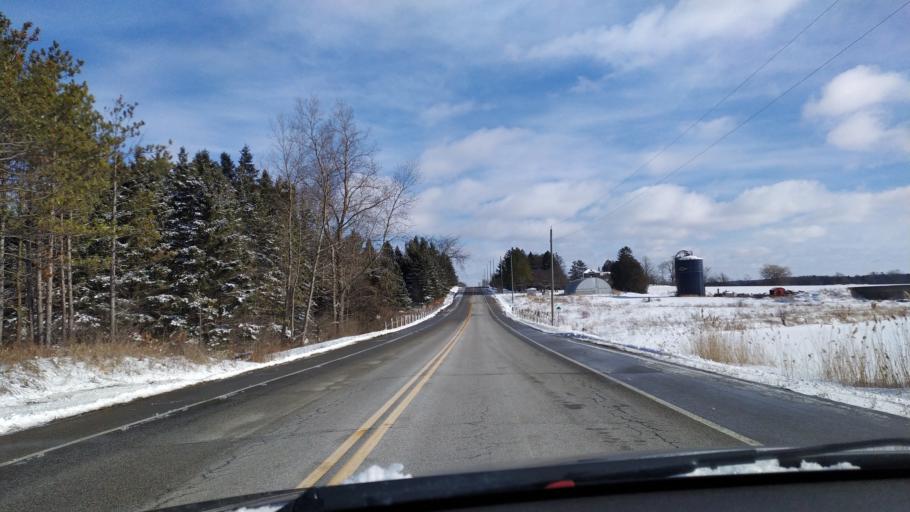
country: CA
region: Ontario
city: Waterloo
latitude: 43.4737
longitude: -80.7111
